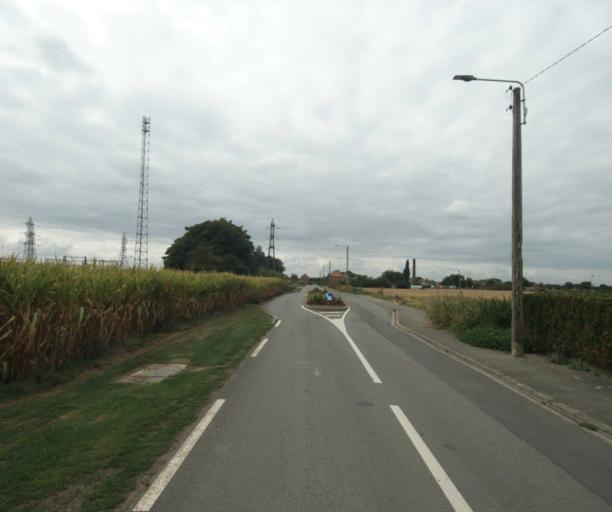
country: FR
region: Nord-Pas-de-Calais
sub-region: Departement du Nord
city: Anstaing
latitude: 50.6068
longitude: 3.1864
